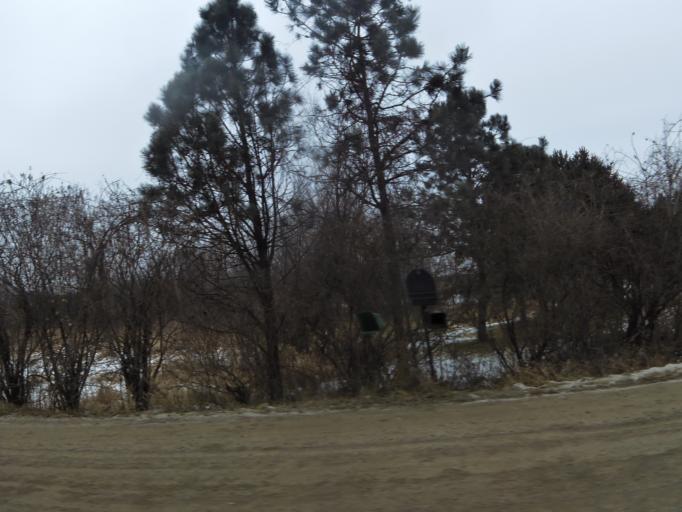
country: US
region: Minnesota
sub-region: Wright County
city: Montrose
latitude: 45.0285
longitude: -93.8572
